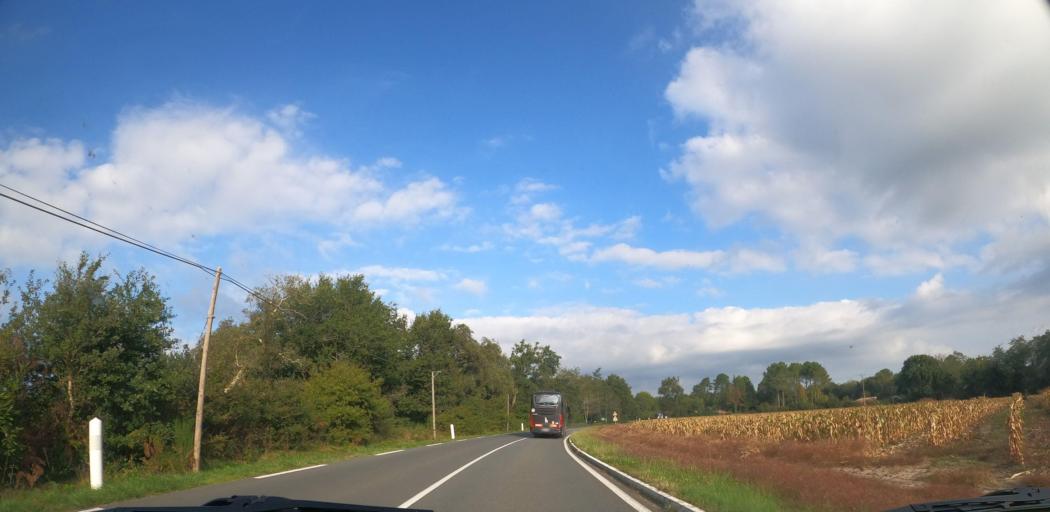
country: FR
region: Aquitaine
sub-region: Departement des Landes
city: Soustons
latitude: 43.7311
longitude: -1.2870
